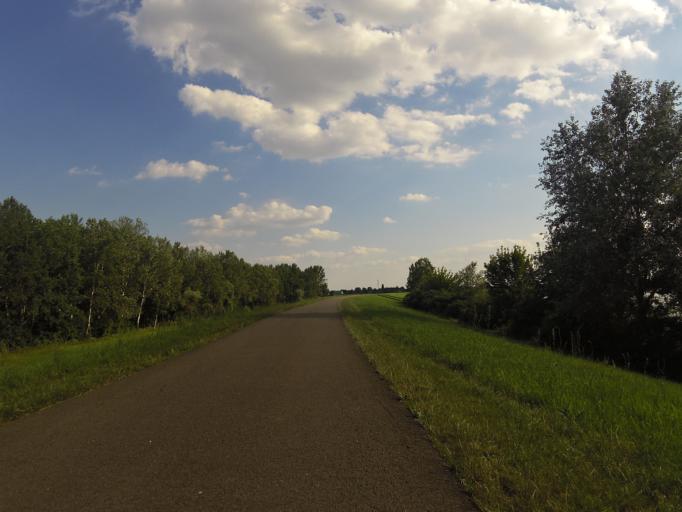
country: HU
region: Jasz-Nagykun-Szolnok
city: Abadszalok
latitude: 47.4917
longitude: 20.6087
